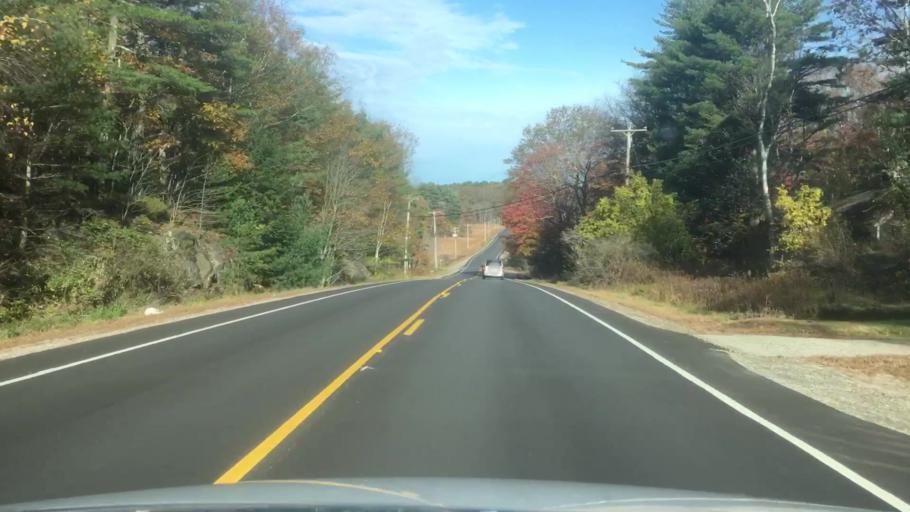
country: US
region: Maine
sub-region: Sagadahoc County
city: Woolwich
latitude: 43.8984
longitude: -69.7953
